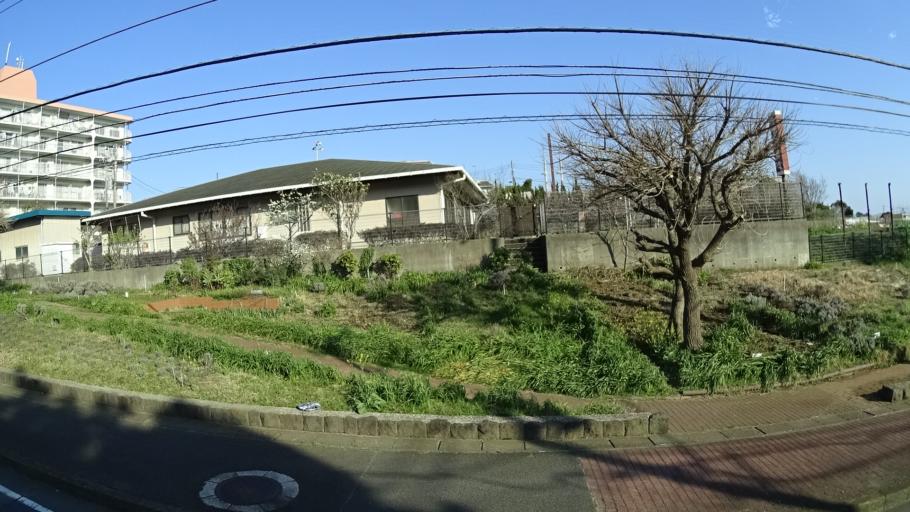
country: JP
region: Kanagawa
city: Miura
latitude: 35.1595
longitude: 139.6391
